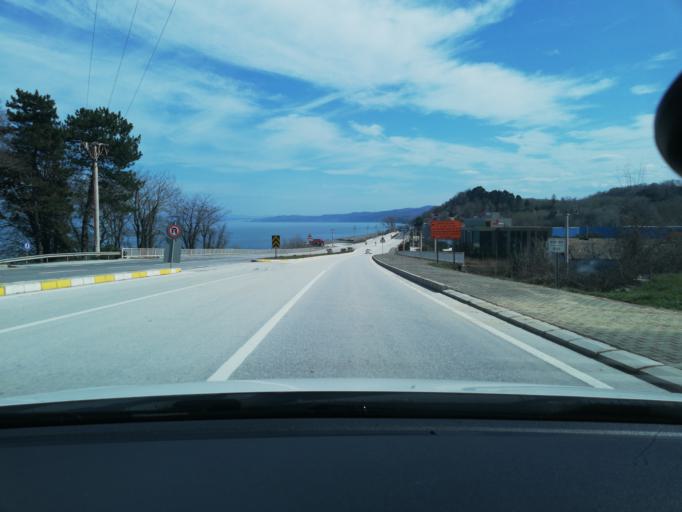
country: TR
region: Duzce
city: Akcakoca
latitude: 41.0943
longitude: 31.1934
